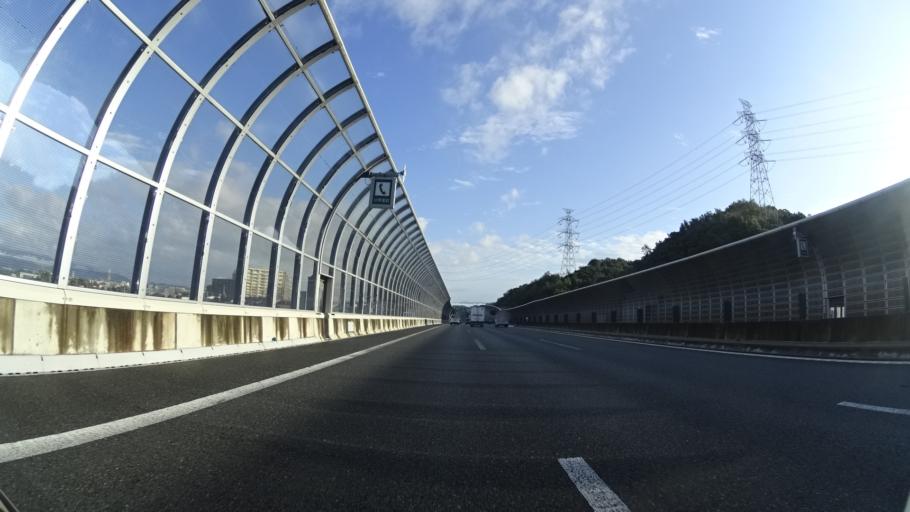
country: JP
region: Osaka
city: Hirakata
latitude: 34.8001
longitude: 135.7049
